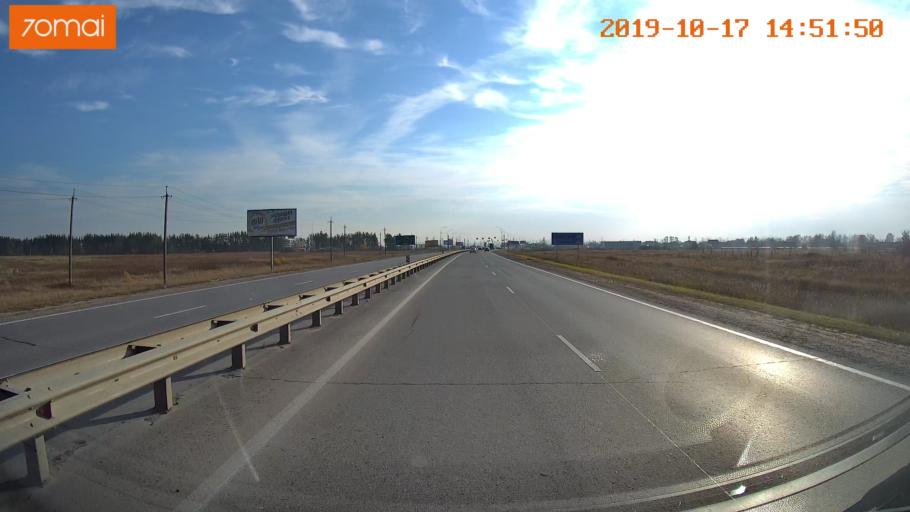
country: RU
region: Rjazan
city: Polyany
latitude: 54.7132
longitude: 39.8478
